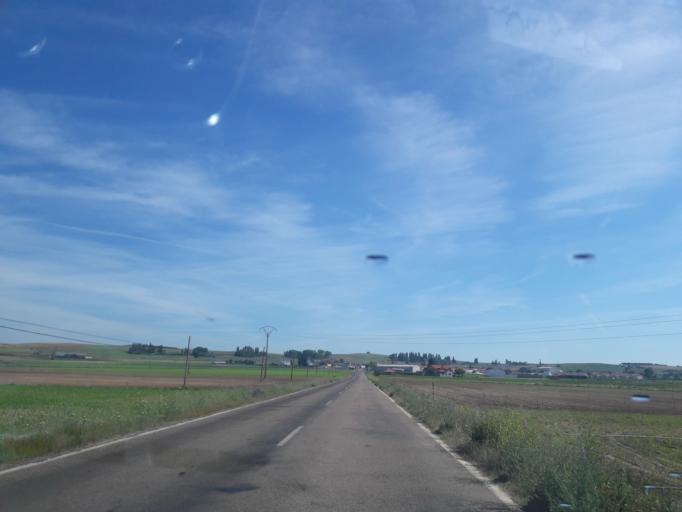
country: ES
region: Castille and Leon
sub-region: Provincia de Salamanca
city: Villoruela
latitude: 40.9977
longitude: -5.4012
